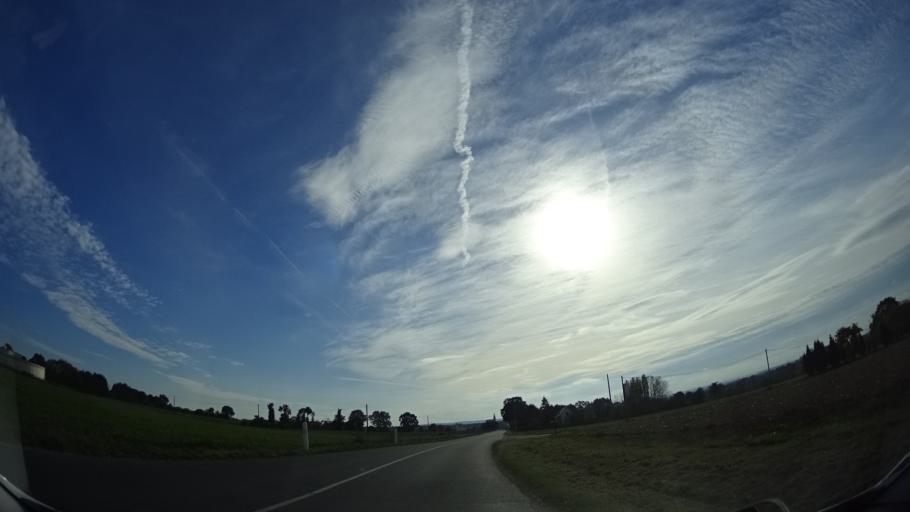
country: FR
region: Brittany
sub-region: Departement d'Ille-et-Vilaine
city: Bedee
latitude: 48.1991
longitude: -1.9395
